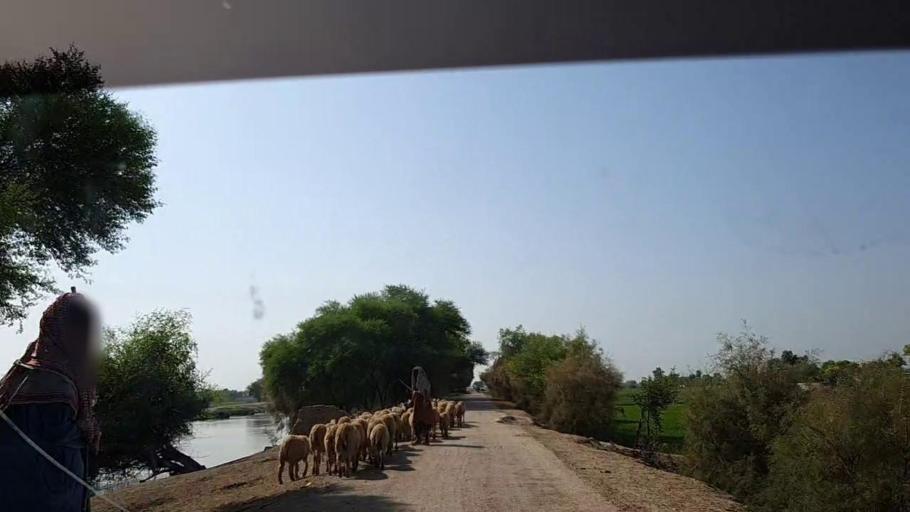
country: PK
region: Sindh
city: Ghauspur
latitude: 28.1938
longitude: 69.0523
